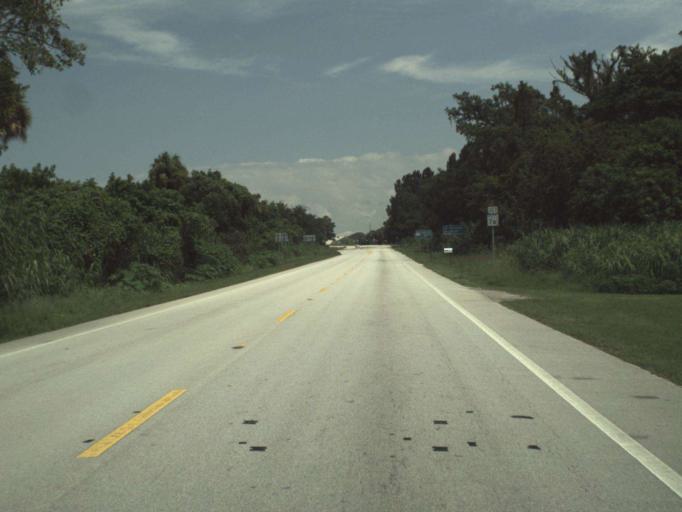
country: US
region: Florida
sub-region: Martin County
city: Indiantown
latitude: 26.9732
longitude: -80.6127
